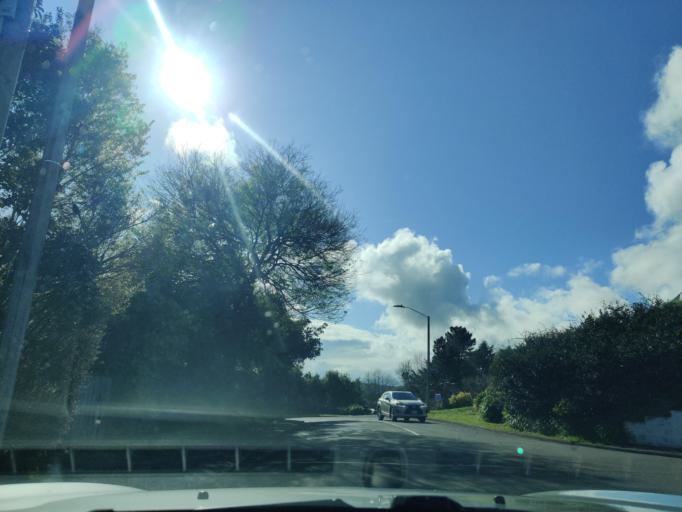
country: NZ
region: Hawke's Bay
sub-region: Hastings District
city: Hastings
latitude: -39.6734
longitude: 176.8944
